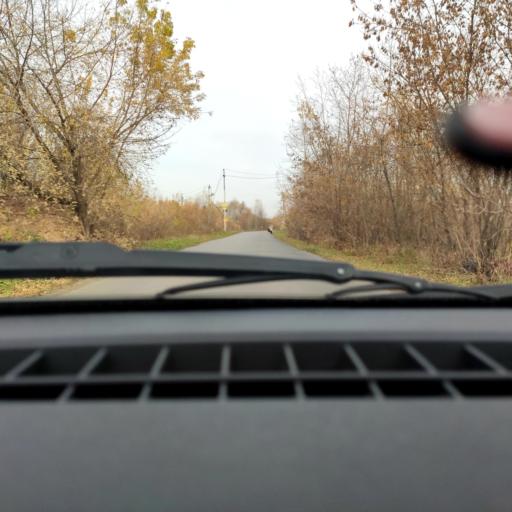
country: RU
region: Bashkortostan
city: Iglino
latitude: 54.8092
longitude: 56.1888
